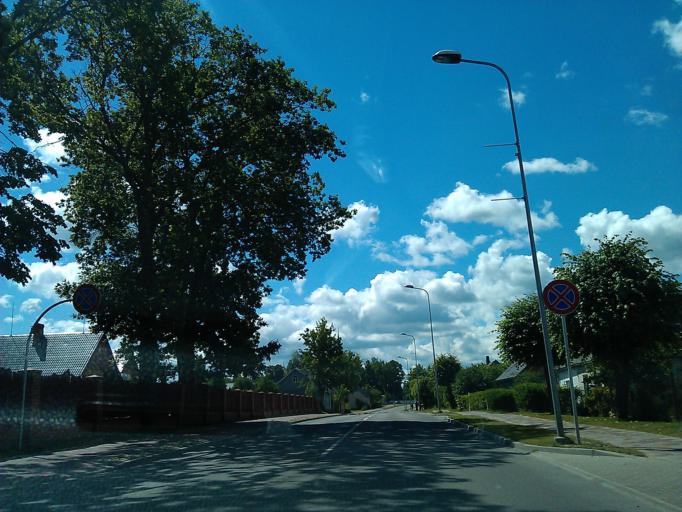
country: LV
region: Vilanu
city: Vilani
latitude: 56.5557
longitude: 26.9240
